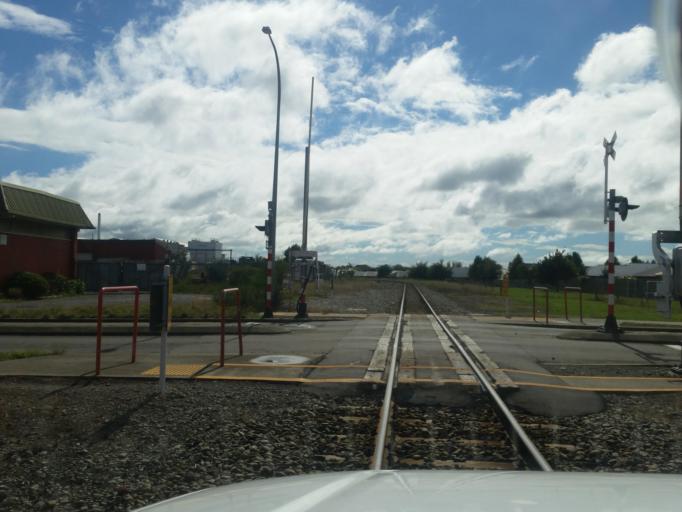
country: NZ
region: Canterbury
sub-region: Waimakariri District
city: Kaiapoi
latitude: -43.3923
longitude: 172.6572
